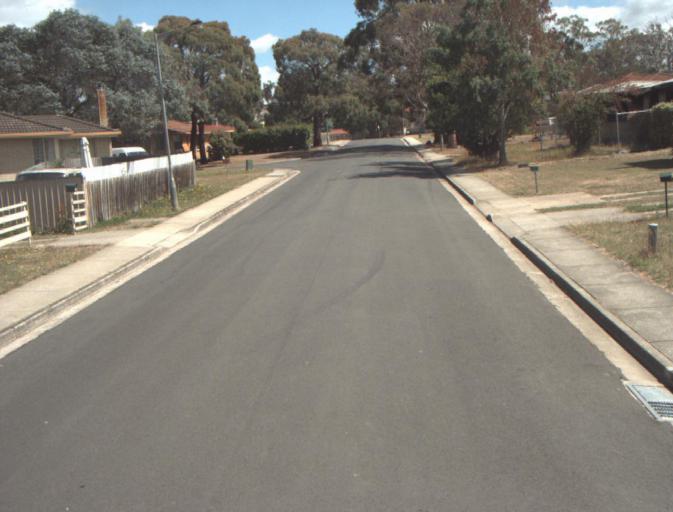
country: AU
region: Tasmania
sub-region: Launceston
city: Newstead
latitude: -41.4124
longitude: 147.1733
